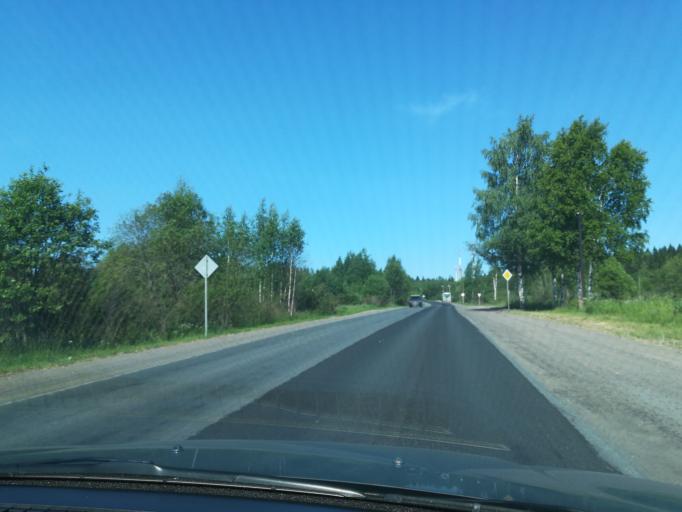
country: RU
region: Leningrad
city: Svetogorsk
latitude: 61.0949
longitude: 28.8877
